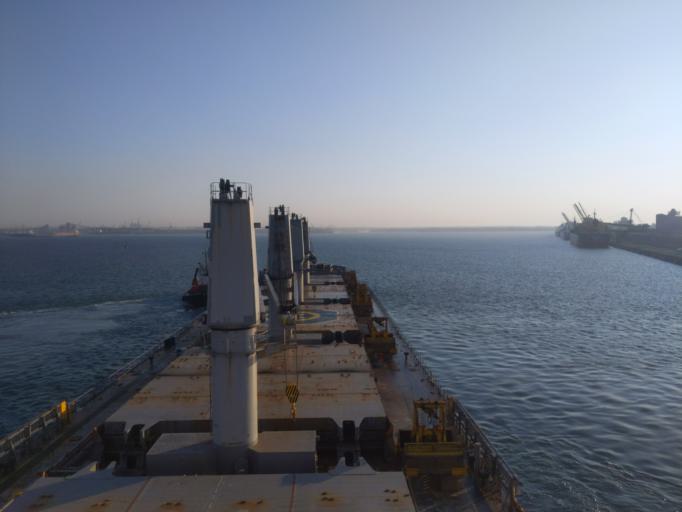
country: ZA
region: KwaZulu-Natal
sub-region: uThungulu District Municipality
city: Richards Bay
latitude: -28.8209
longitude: 32.0459
